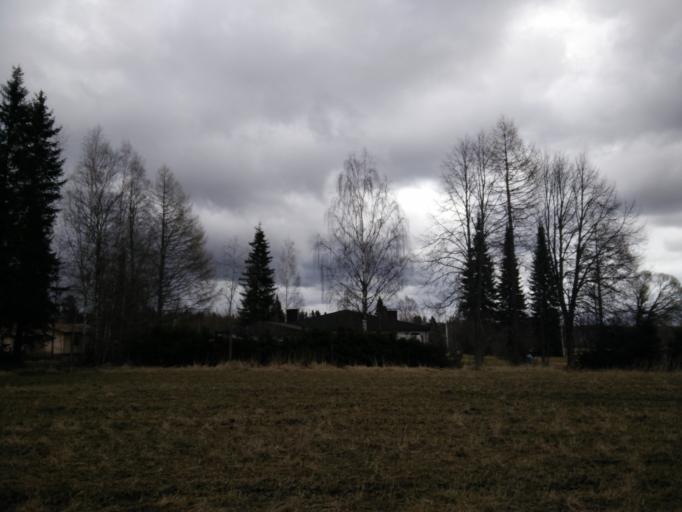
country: FI
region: Pirkanmaa
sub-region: Tampere
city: Orivesi
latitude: 61.6907
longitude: 24.3564
